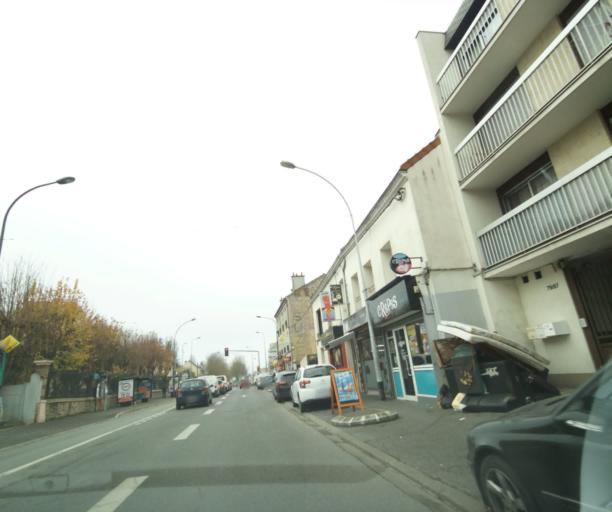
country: FR
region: Ile-de-France
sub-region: Departement de Seine-Saint-Denis
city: Vaujours
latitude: 48.9348
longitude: 2.5676
